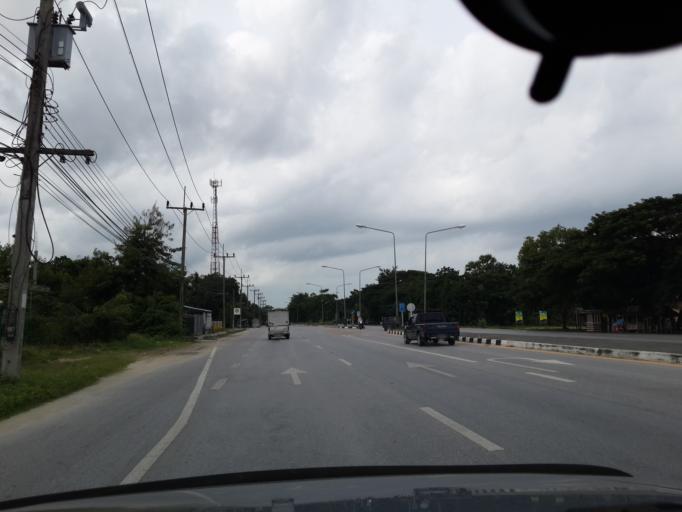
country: TH
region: Pattani
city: Yaring
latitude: 6.8730
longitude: 101.3112
